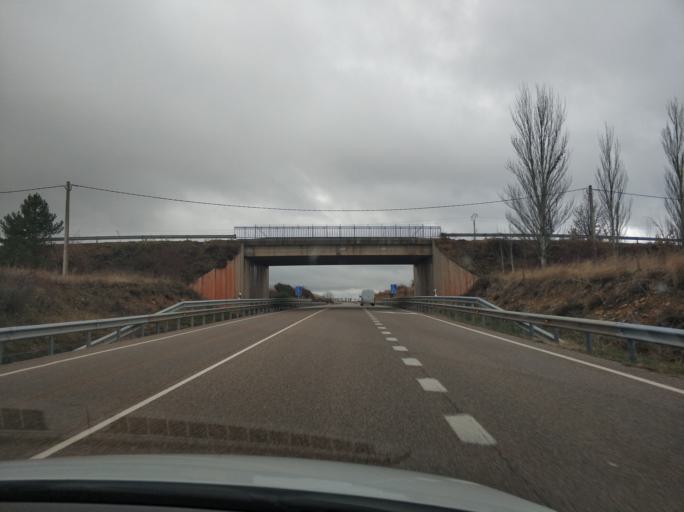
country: ES
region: Castille and Leon
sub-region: Provincia de Segovia
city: Riaza
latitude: 41.2887
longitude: -3.4844
